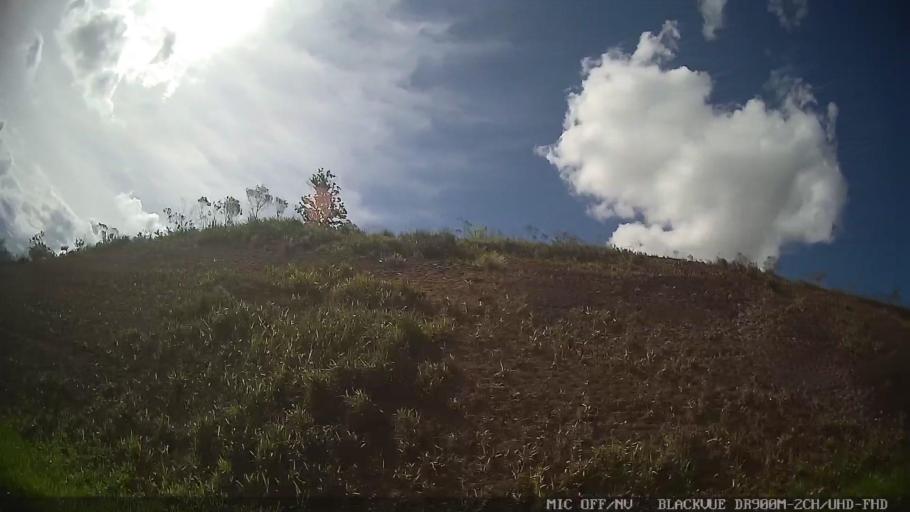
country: BR
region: Sao Paulo
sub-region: Pedreira
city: Pedreira
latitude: -22.7332
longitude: -46.8633
